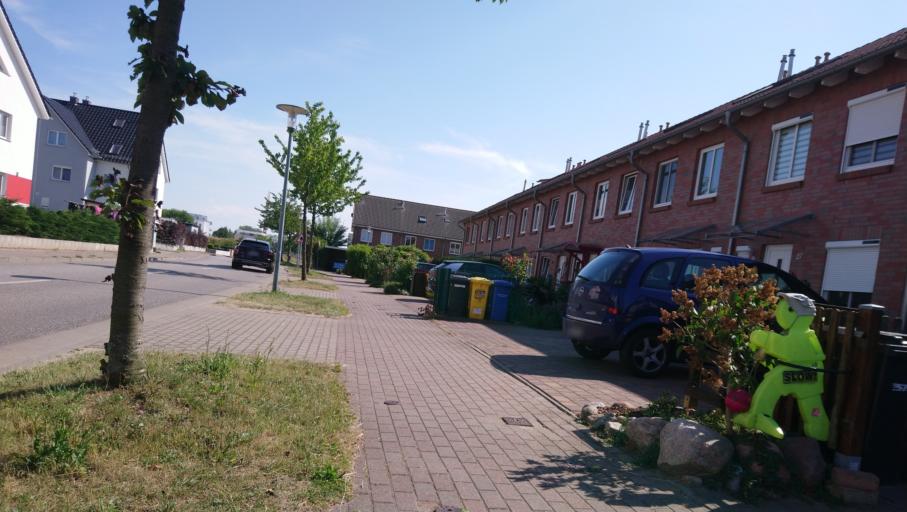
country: DE
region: Mecklenburg-Vorpommern
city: Roggentin
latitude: 54.0884
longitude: 12.1882
